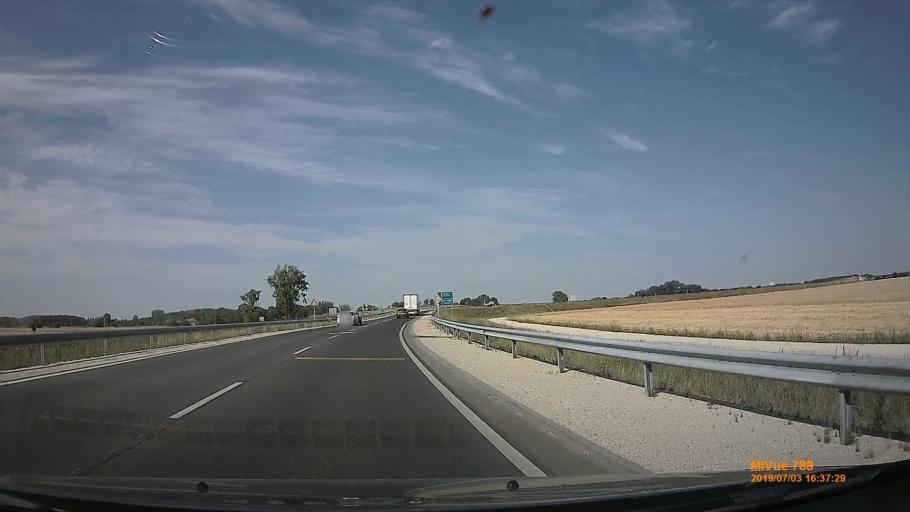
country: HU
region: Gyor-Moson-Sopron
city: Gyor
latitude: 47.7367
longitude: 17.6422
